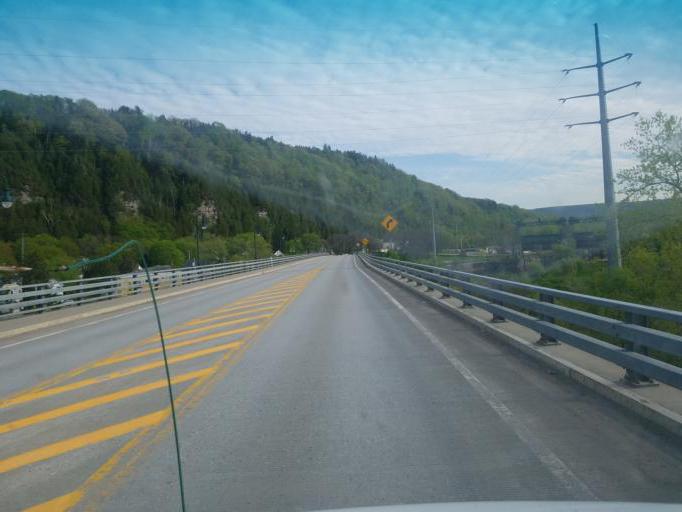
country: US
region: New York
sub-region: Herkimer County
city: Little Falls
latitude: 43.0398
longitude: -74.8607
